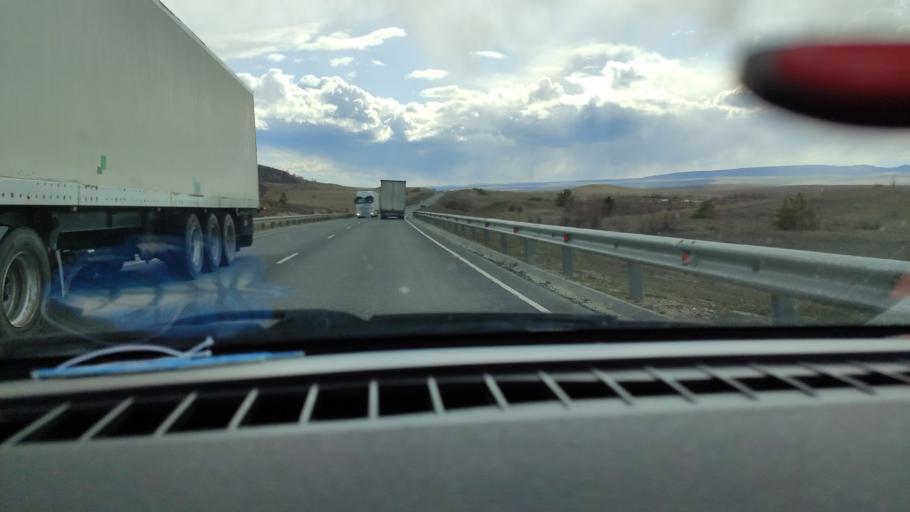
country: RU
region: Saratov
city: Alekseyevka
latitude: 52.3649
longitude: 47.9600
